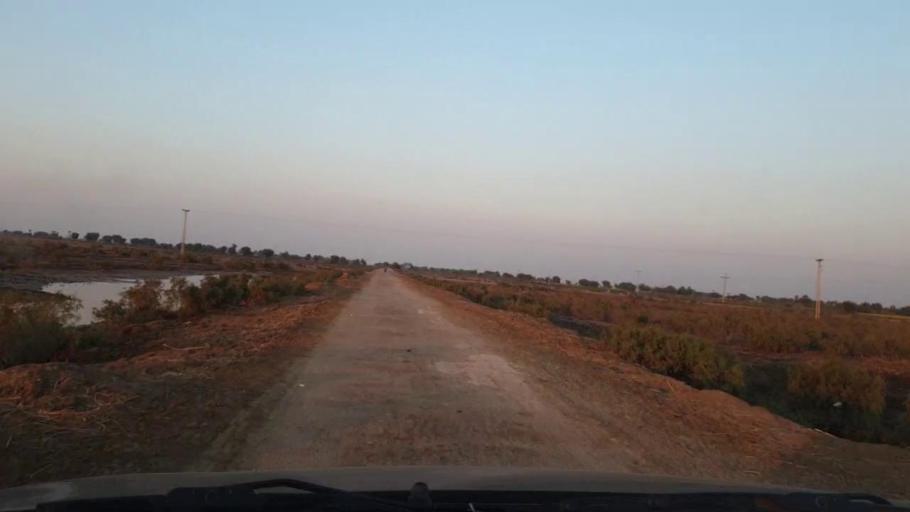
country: PK
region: Sindh
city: Jhol
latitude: 25.9297
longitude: 68.9671
